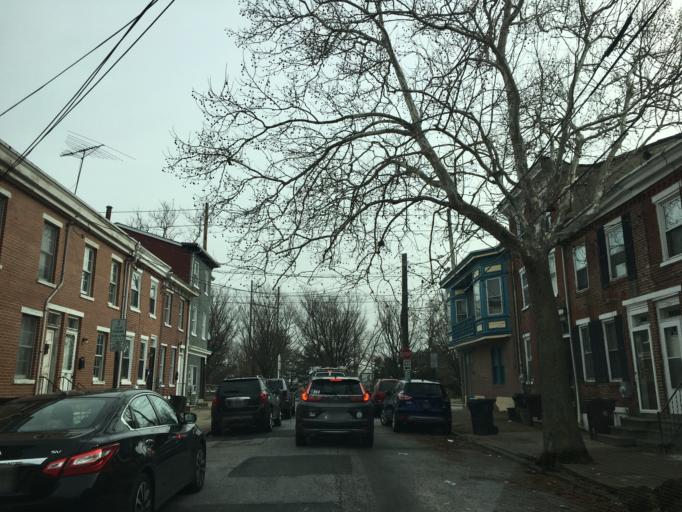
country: US
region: Delaware
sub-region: New Castle County
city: Wilmington
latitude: 39.7386
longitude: -75.5421
